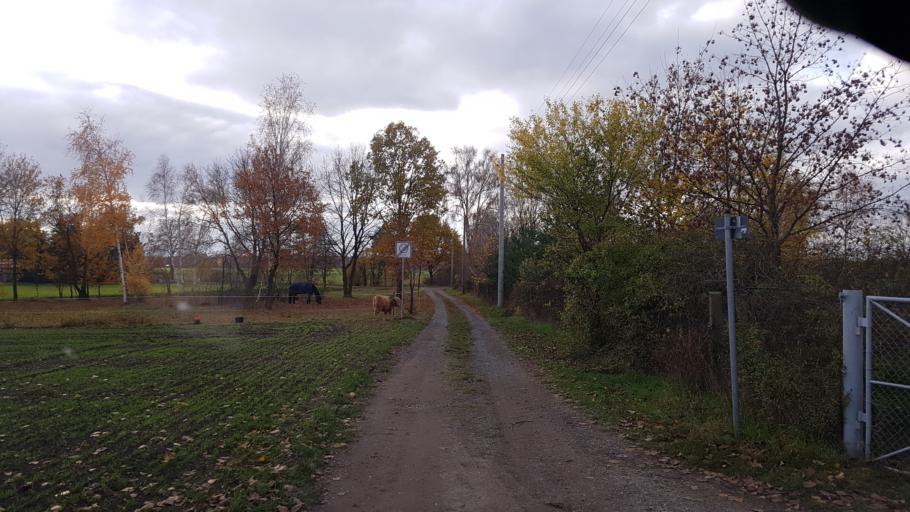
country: DE
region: Brandenburg
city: Sallgast
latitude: 51.6024
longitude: 13.8566
